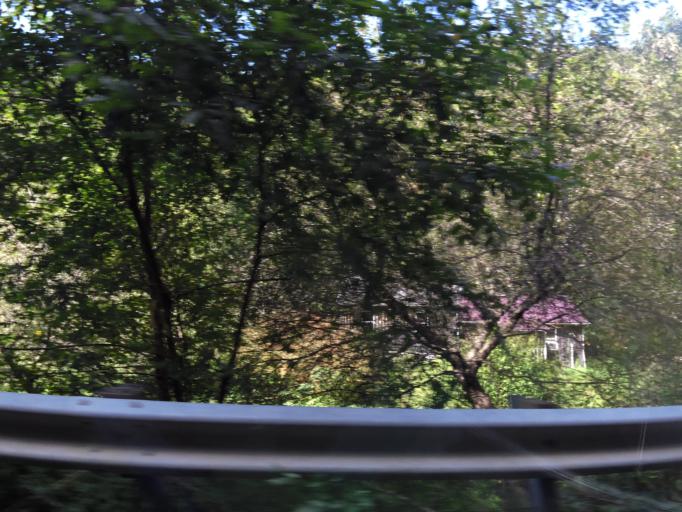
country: US
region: Kentucky
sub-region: Leslie County
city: Hyden
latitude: 37.0186
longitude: -83.3972
